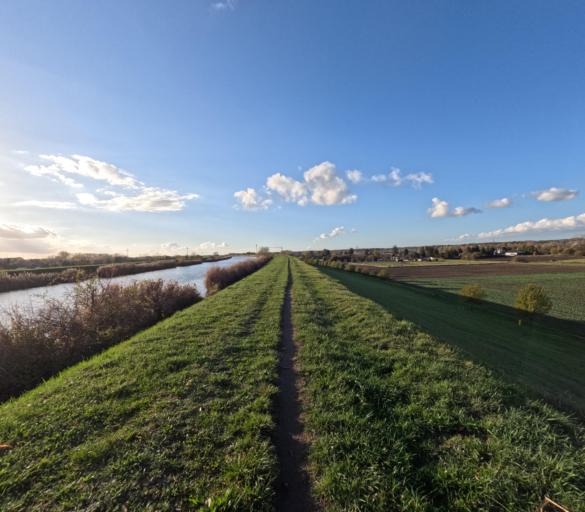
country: DE
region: Saxony
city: Schkeuditz
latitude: 51.3584
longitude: 12.2171
